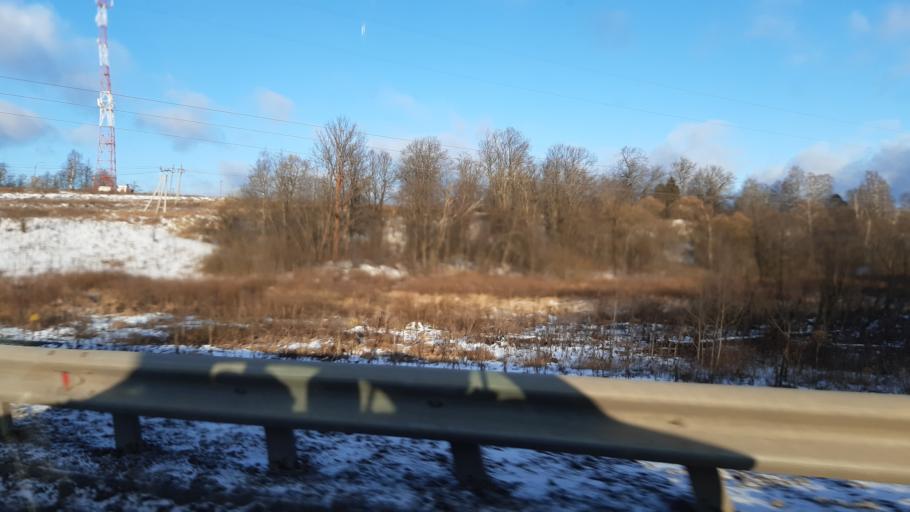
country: RU
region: Vladimir
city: Arsaki
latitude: 56.2831
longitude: 38.3973
